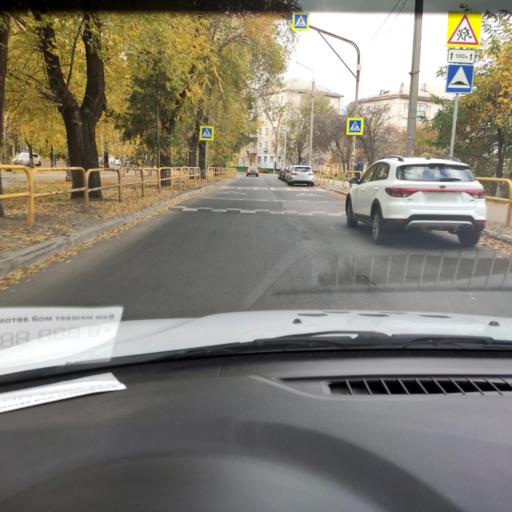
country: RU
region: Samara
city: Tol'yatti
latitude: 53.5163
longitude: 49.4202
